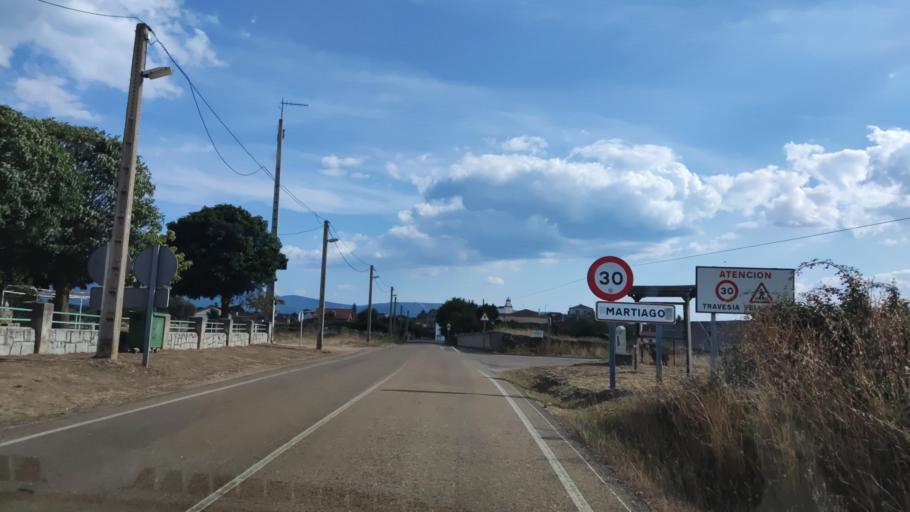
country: ES
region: Castille and Leon
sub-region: Provincia de Salamanca
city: Martiago
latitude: 40.4574
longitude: -6.4901
